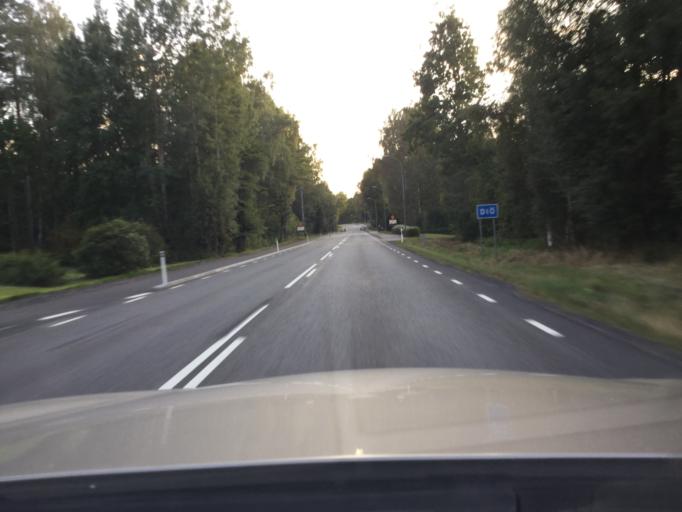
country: SE
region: Kronoberg
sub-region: Almhults Kommun
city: AElmhult
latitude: 56.6501
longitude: 14.2367
